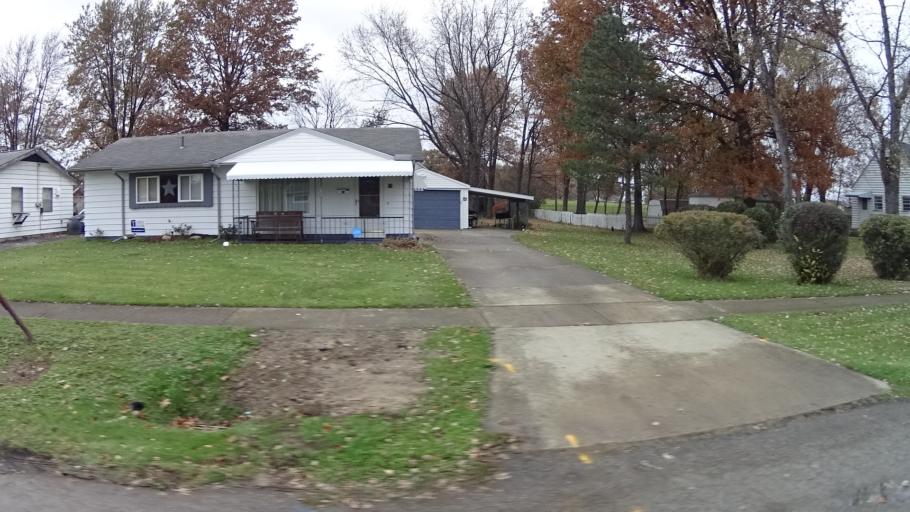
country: US
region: Ohio
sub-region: Lorain County
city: Elyria
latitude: 41.3828
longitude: -82.1200
